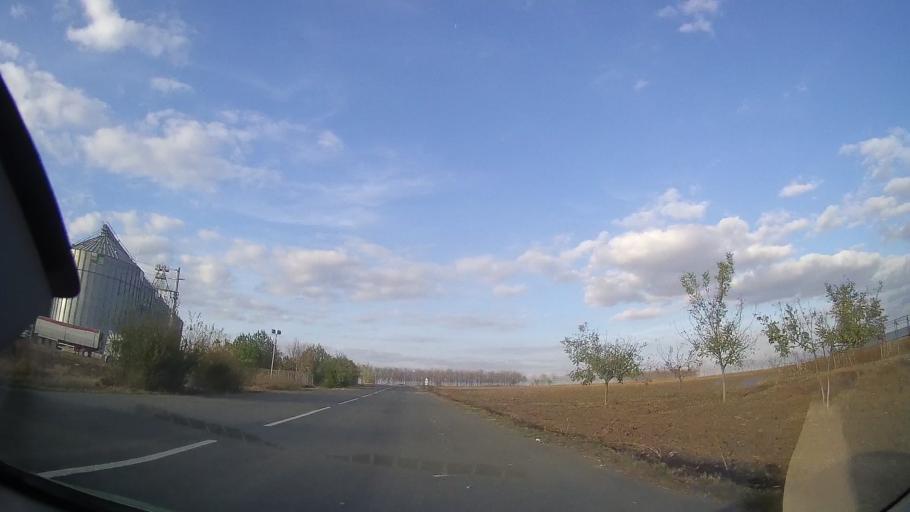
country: RO
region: Constanta
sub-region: Comuna Dumbraveni
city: Dumbraveni
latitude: 43.9263
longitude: 28.0297
